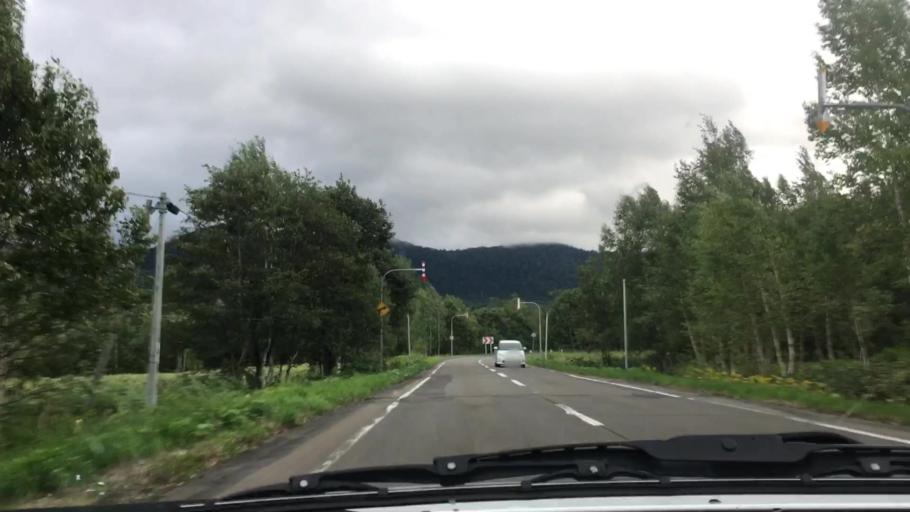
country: JP
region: Hokkaido
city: Shimo-furano
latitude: 43.0538
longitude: 142.6692
